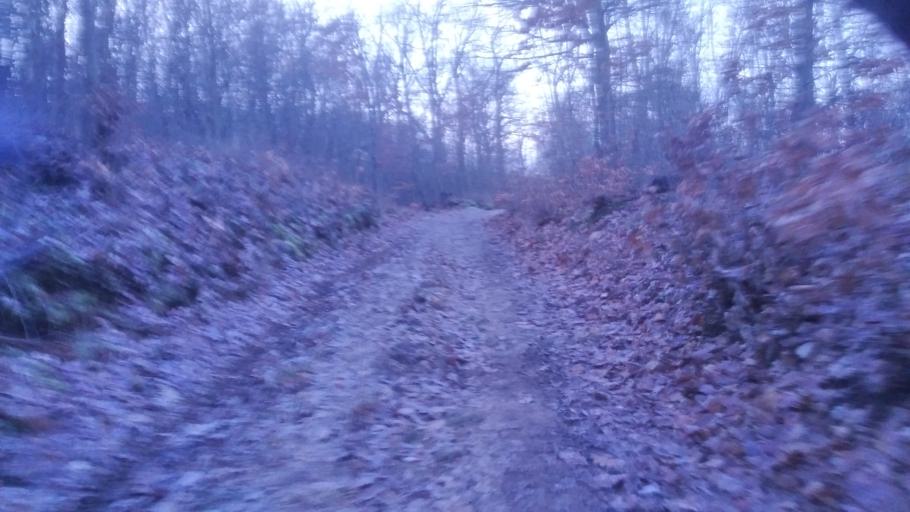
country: HU
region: Pest
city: Pilisborosjeno
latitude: 47.6155
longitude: 19.0028
